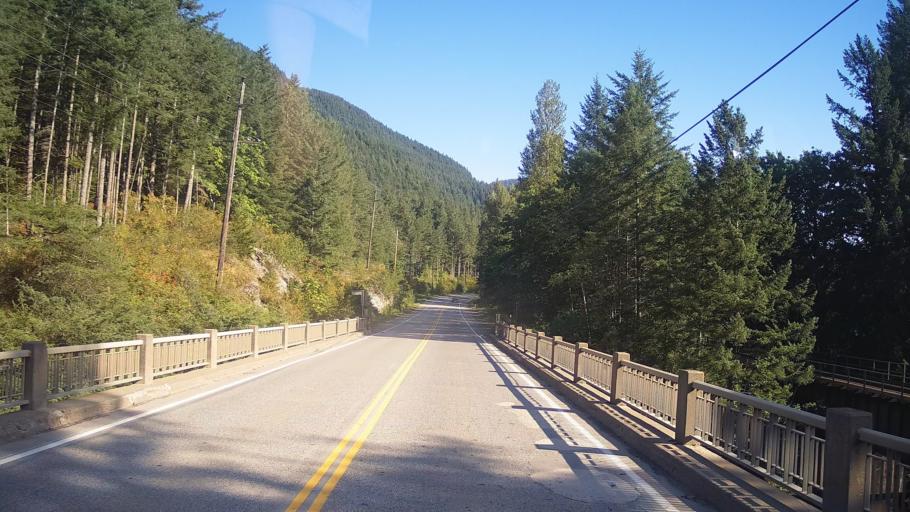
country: CA
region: British Columbia
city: Hope
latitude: 49.4306
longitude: -121.4382
